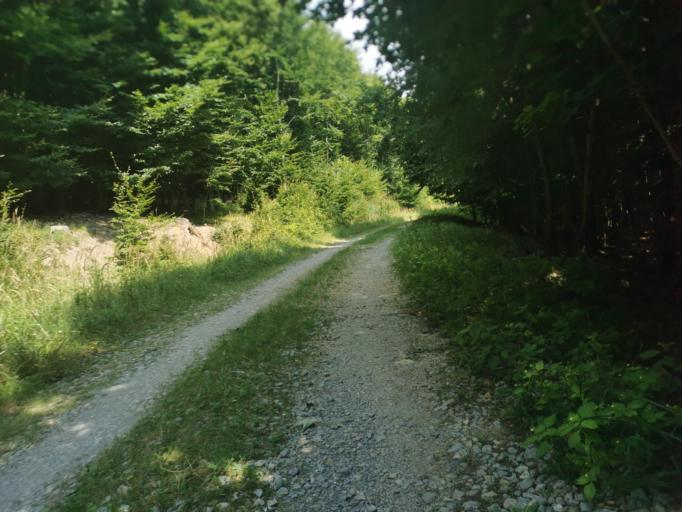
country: SK
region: Trenciansky
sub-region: Okres Myjava
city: Myjava
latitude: 48.8231
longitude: 17.5860
